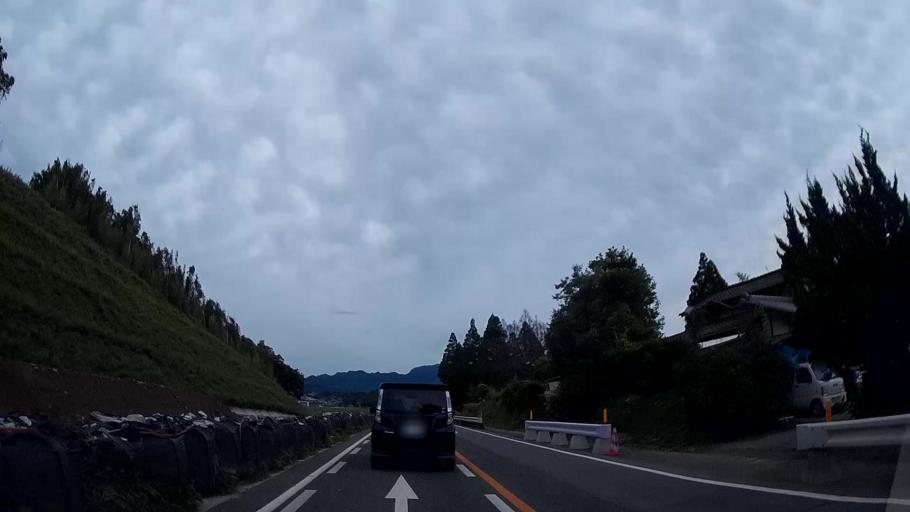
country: JP
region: Kumamoto
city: Kikuchi
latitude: 32.9558
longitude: 130.8220
